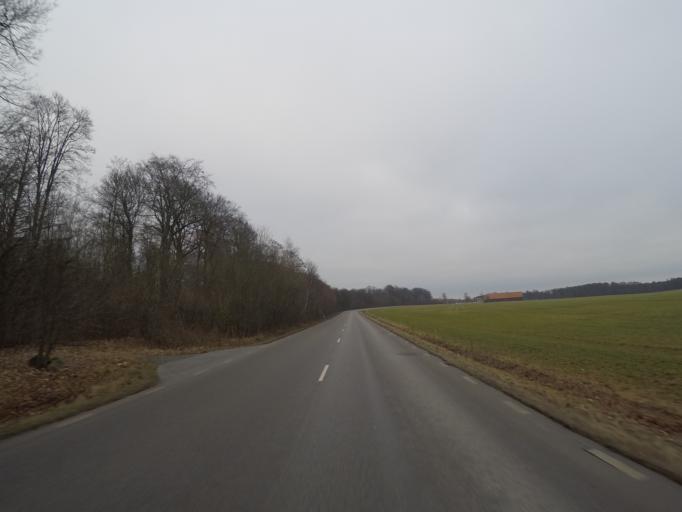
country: SE
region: Skane
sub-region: Hoors Kommun
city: Loberod
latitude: 55.7713
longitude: 13.4697
